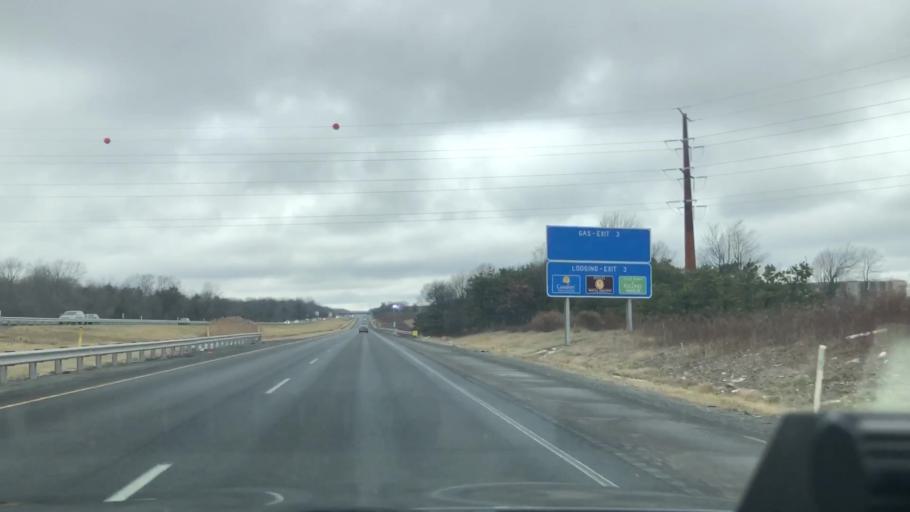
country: US
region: Pennsylvania
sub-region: Monroe County
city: Emerald Lakes
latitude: 41.0913
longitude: -75.3958
